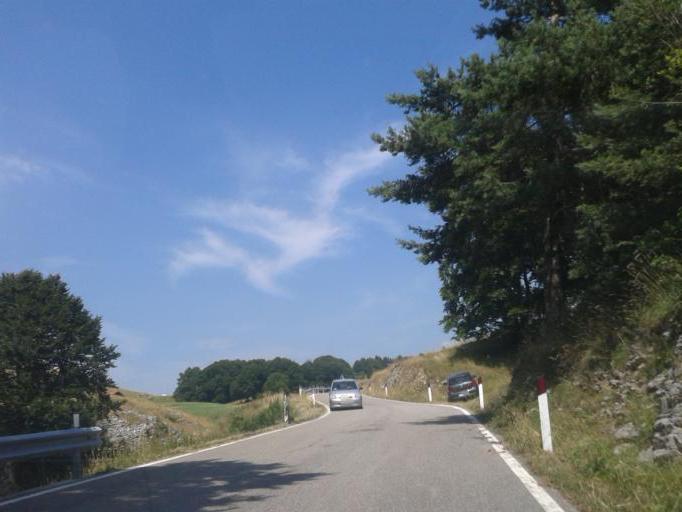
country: IT
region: Trentino-Alto Adige
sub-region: Provincia di Trento
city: Avio
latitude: 45.7787
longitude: 10.9089
